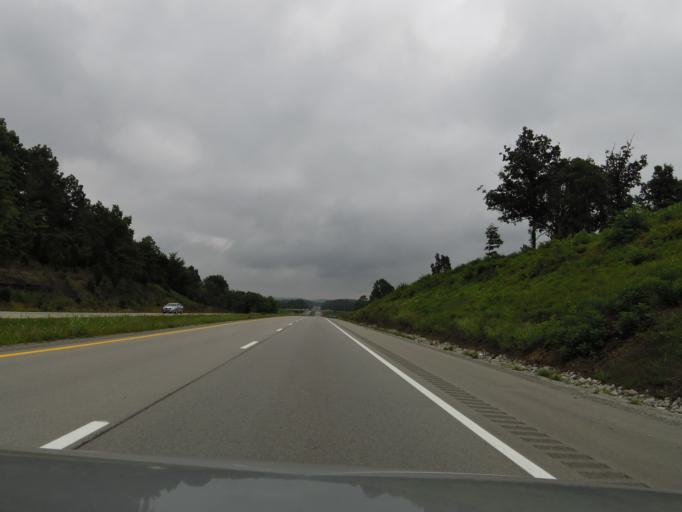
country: US
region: Kentucky
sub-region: Grayson County
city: Leitchfield
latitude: 37.4123
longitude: -86.4932
